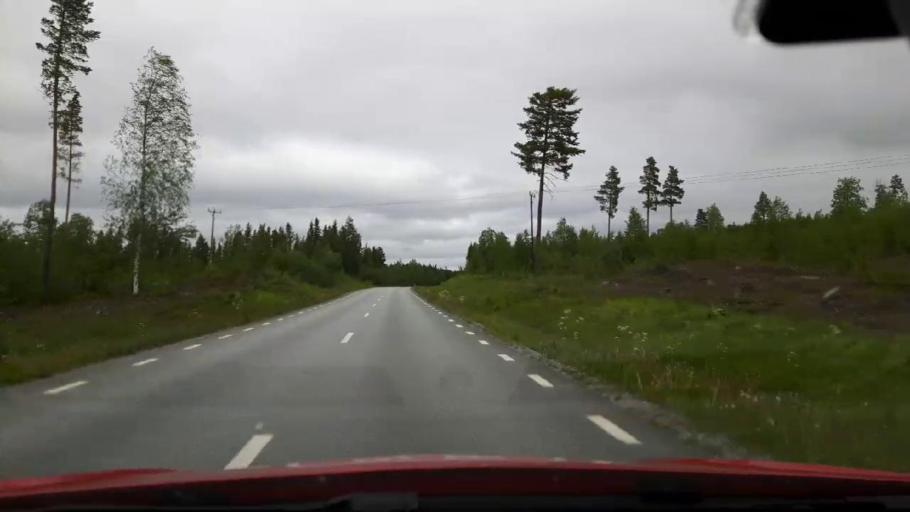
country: SE
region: Jaemtland
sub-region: OEstersunds Kommun
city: Lit
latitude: 63.7228
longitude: 14.7177
